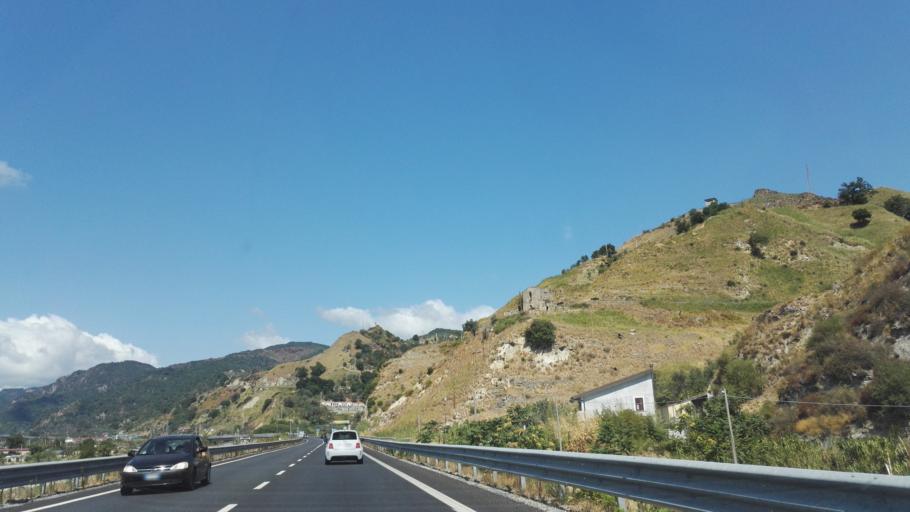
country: IT
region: Calabria
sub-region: Provincia di Reggio Calabria
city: Mammola
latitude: 38.3538
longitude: 16.2444
